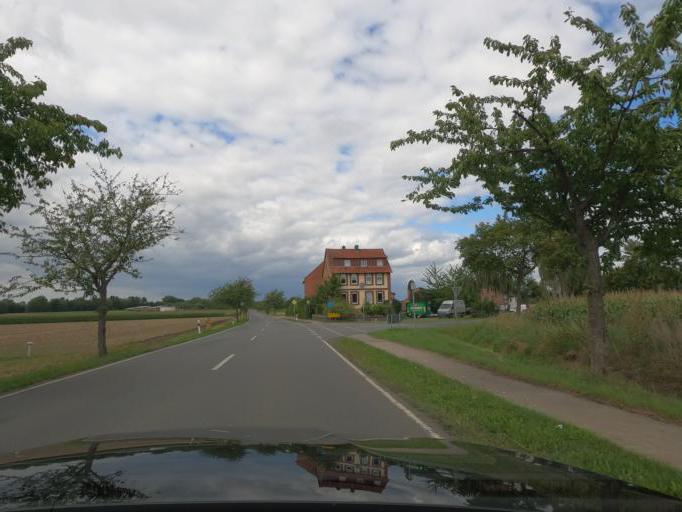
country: DE
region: Lower Saxony
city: Algermissen
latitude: 52.2609
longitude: 9.9626
